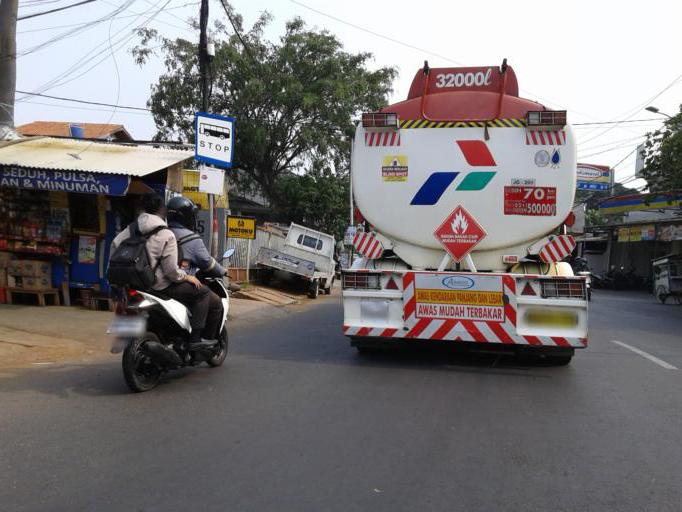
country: ID
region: West Java
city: Pamulang
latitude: -6.3097
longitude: 106.7811
